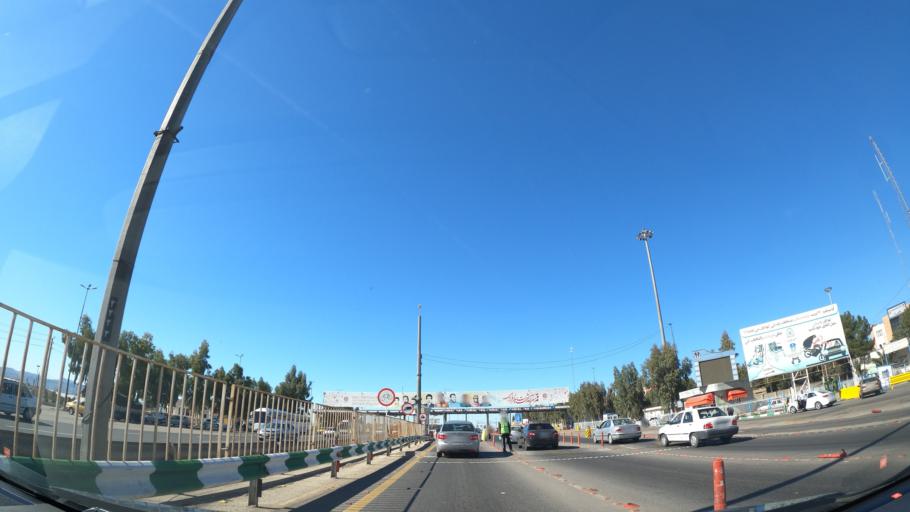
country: IR
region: Qom
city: Qom
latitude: 34.6851
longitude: 50.8912
